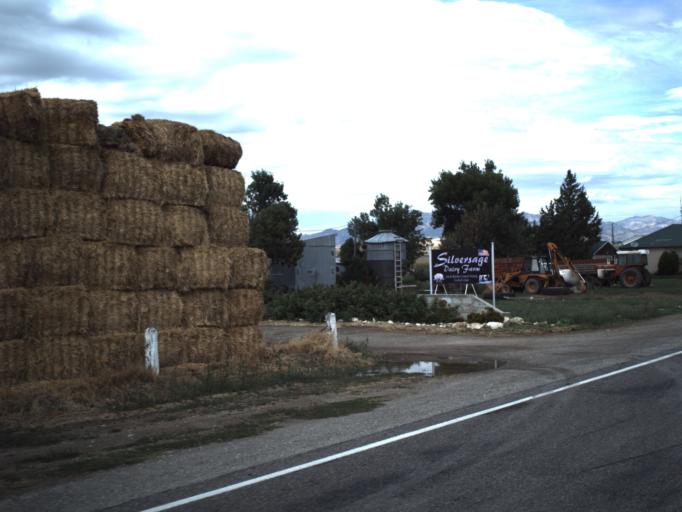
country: US
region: Utah
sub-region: Cache County
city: Lewiston
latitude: 41.9966
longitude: -111.9549
